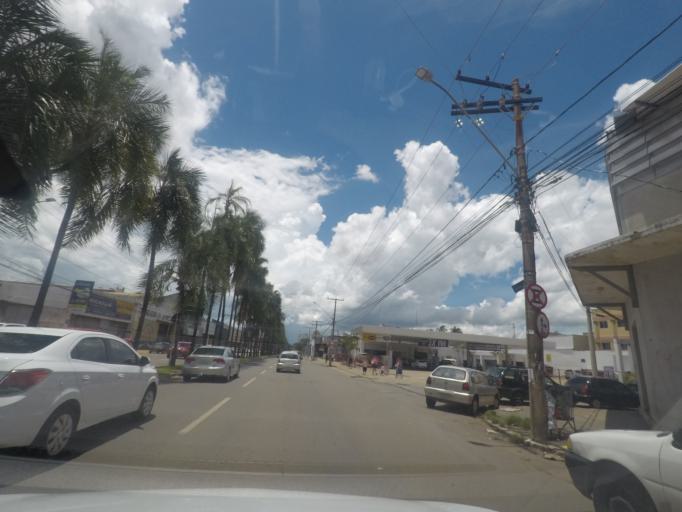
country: BR
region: Goias
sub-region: Goiania
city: Goiania
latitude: -16.6636
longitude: -49.2590
